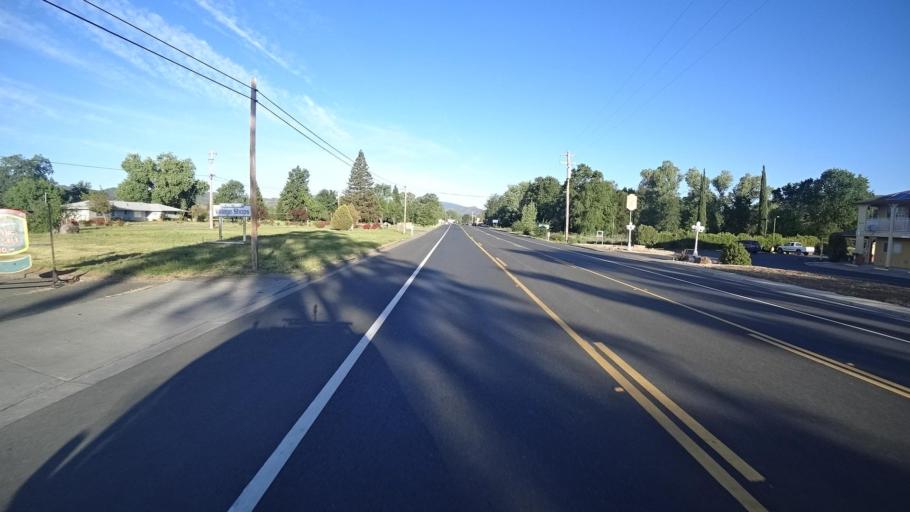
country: US
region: California
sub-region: Lake County
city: Upper Lake
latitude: 39.1619
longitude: -122.9084
